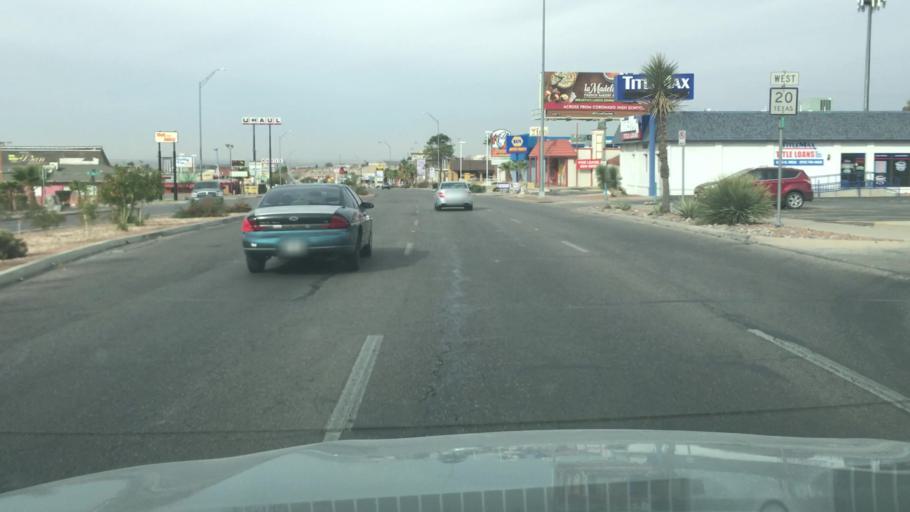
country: US
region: New Mexico
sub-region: Dona Ana County
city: Sunland Park
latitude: 31.8320
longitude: -106.5330
